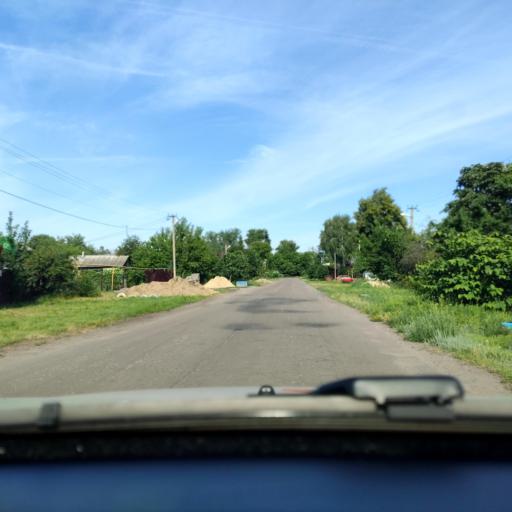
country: RU
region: Voronezj
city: Maslovka
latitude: 51.5366
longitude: 39.2379
